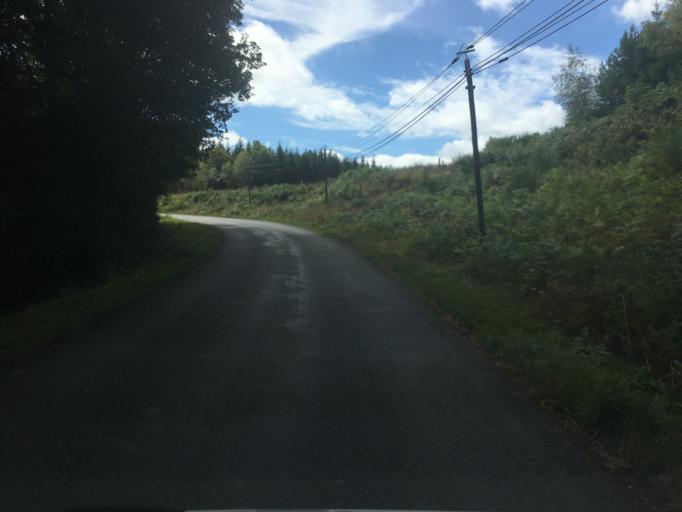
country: FR
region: Limousin
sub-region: Departement de la Correze
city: Neuvic
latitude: 45.4245
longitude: 2.3461
